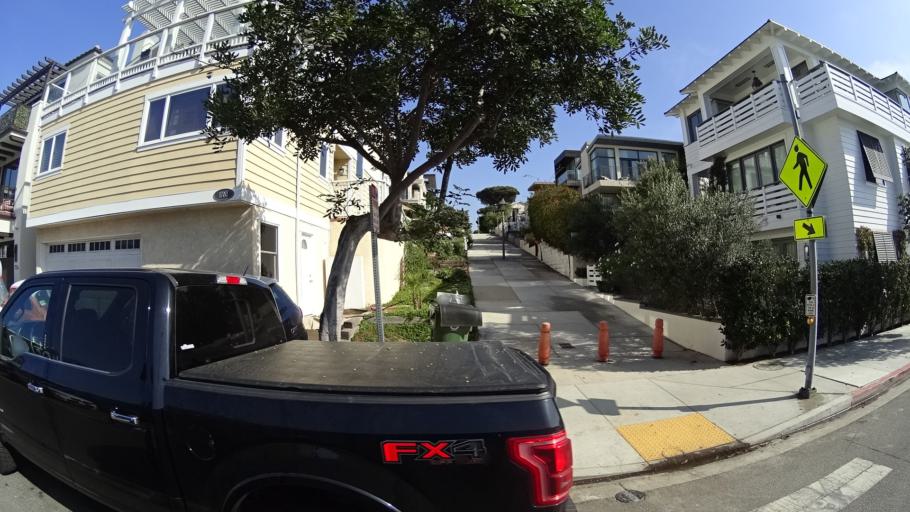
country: US
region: California
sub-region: Los Angeles County
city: Manhattan Beach
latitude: 33.8887
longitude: -118.4119
